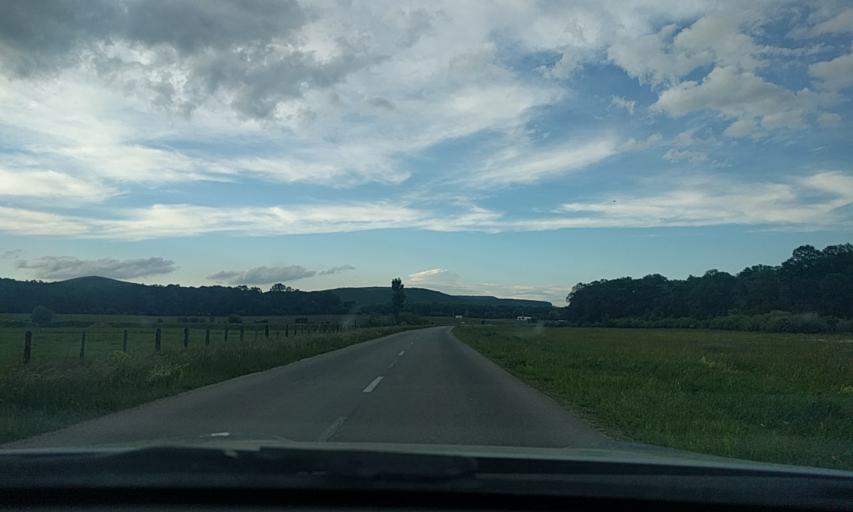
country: RO
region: Brasov
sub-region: Comuna Harman
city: Harman
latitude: 45.7439
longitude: 25.7039
